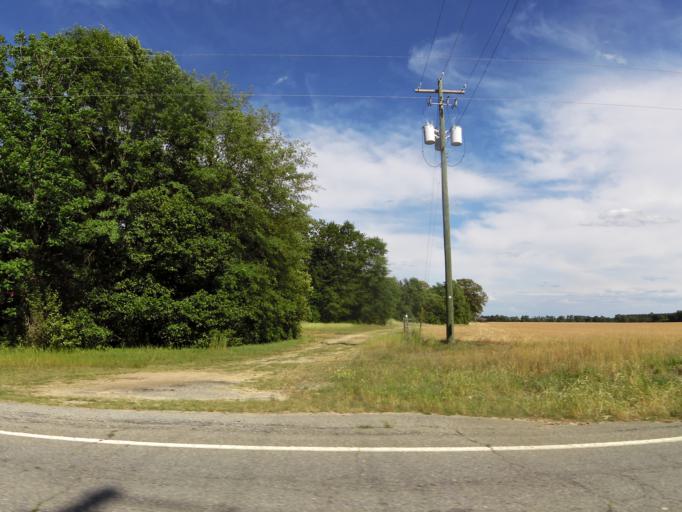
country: US
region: South Carolina
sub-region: Bamberg County
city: Denmark
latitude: 33.1991
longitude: -81.1783
